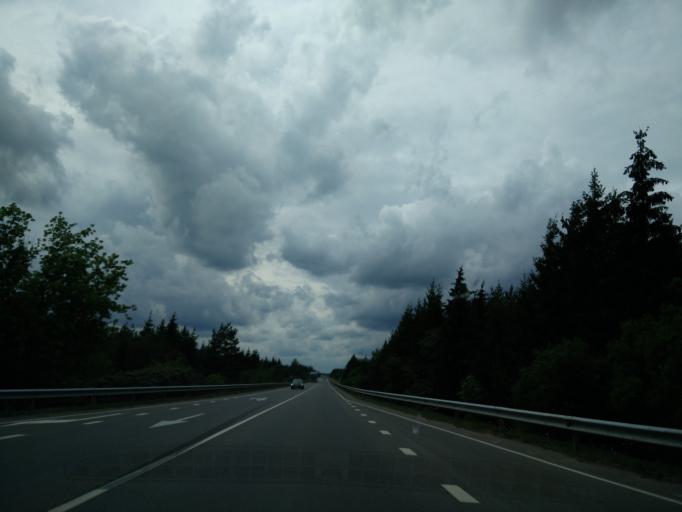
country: LT
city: Lentvaris
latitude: 54.6251
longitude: 24.9955
